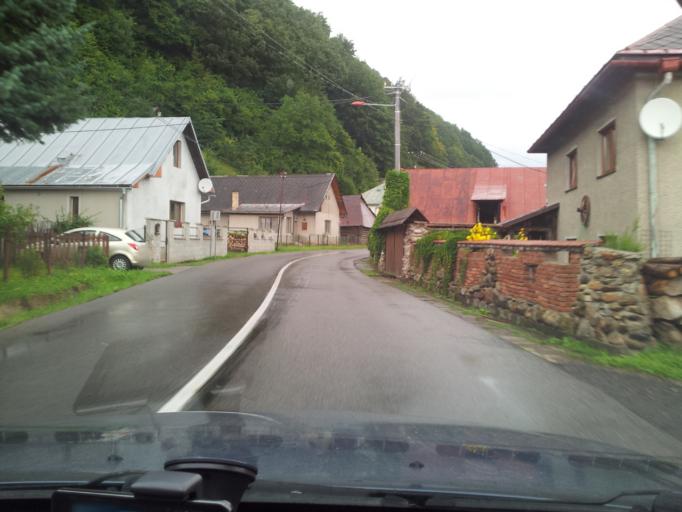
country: SK
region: Banskobystricky
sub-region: Okres Banska Bystrica
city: Brezno
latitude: 48.8544
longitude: 19.6330
